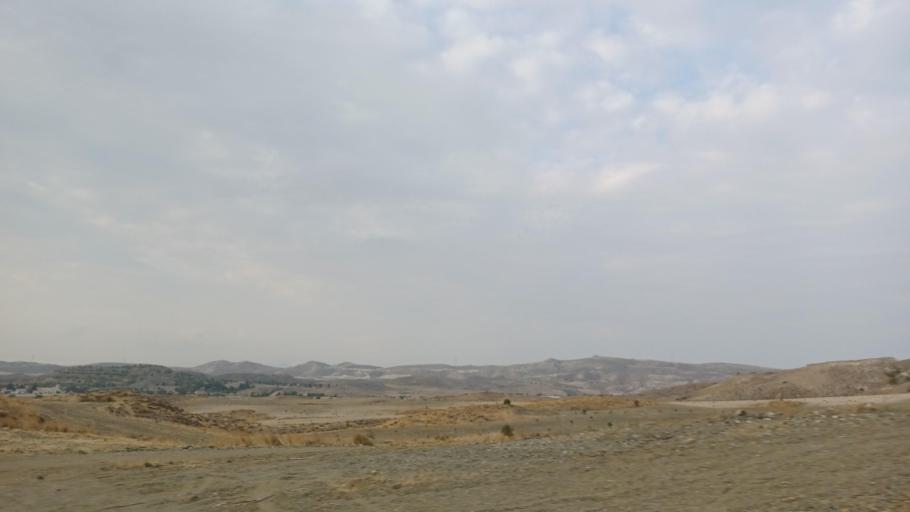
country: CY
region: Larnaka
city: Troulloi
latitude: 35.0191
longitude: 33.5741
